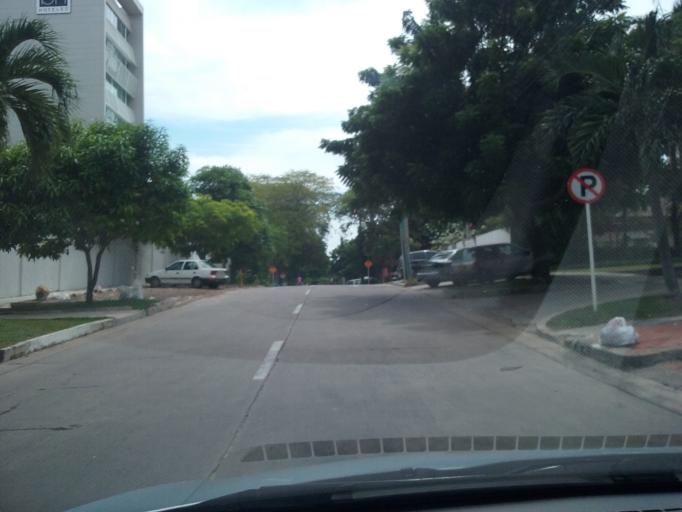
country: CO
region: Atlantico
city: Barranquilla
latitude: 11.0046
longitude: -74.8023
